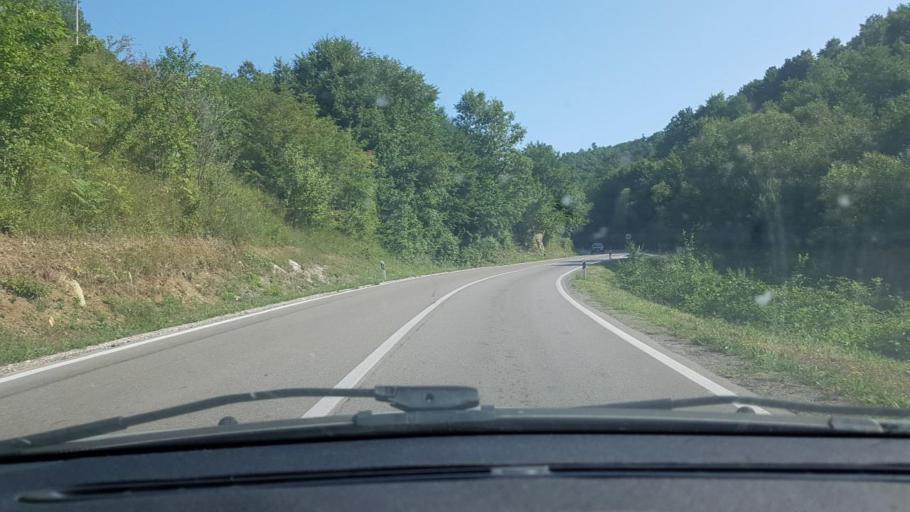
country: BA
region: Federation of Bosnia and Herzegovina
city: Skokovi
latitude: 45.0123
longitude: 15.9026
